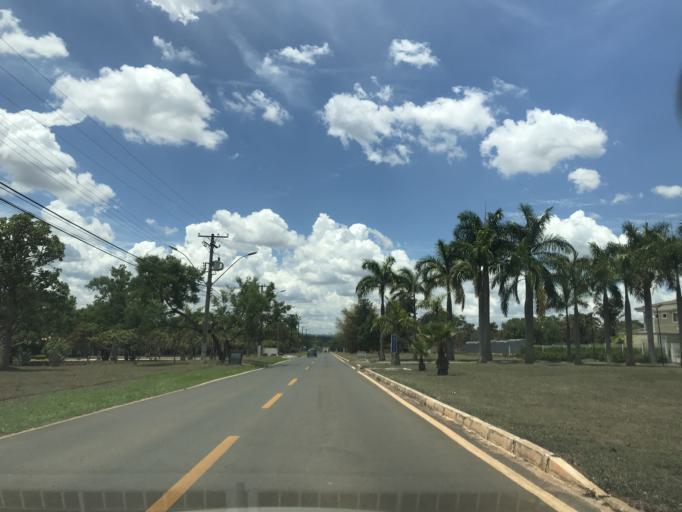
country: BR
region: Federal District
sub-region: Brasilia
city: Brasilia
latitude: -15.9066
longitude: -47.9458
